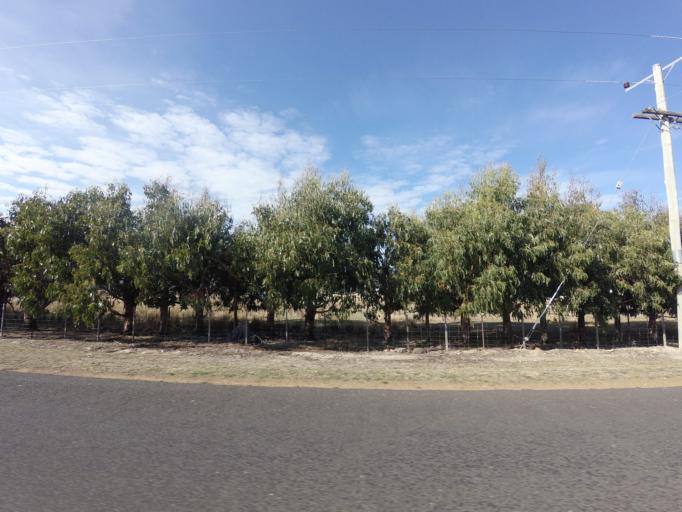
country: AU
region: Tasmania
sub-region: Sorell
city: Sorell
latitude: -42.4633
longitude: 147.4613
